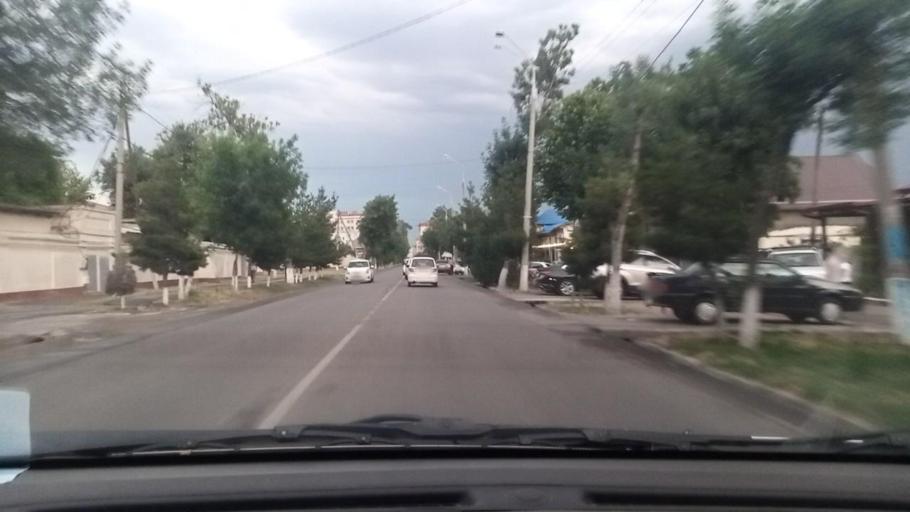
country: UZ
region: Toshkent Shahri
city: Tashkent
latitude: 41.2839
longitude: 69.2839
